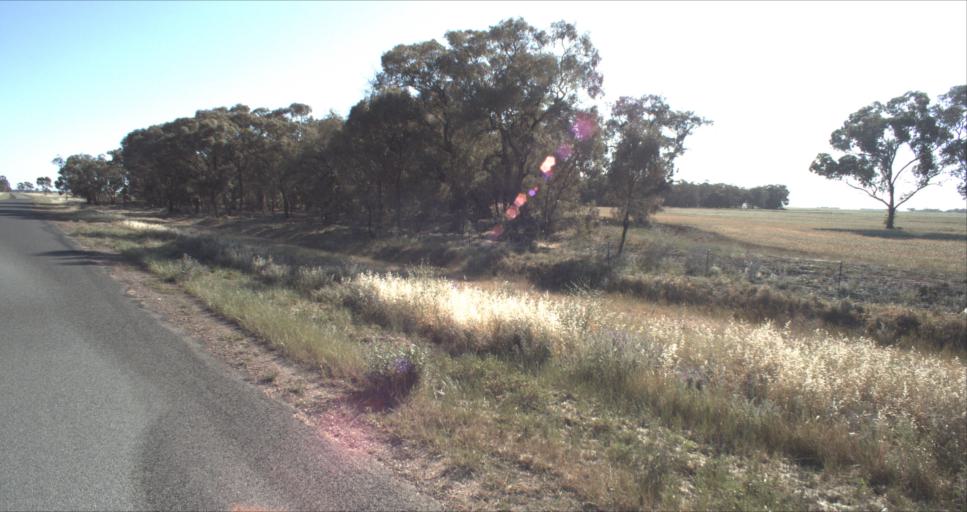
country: AU
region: New South Wales
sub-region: Leeton
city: Leeton
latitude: -34.5643
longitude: 146.2647
